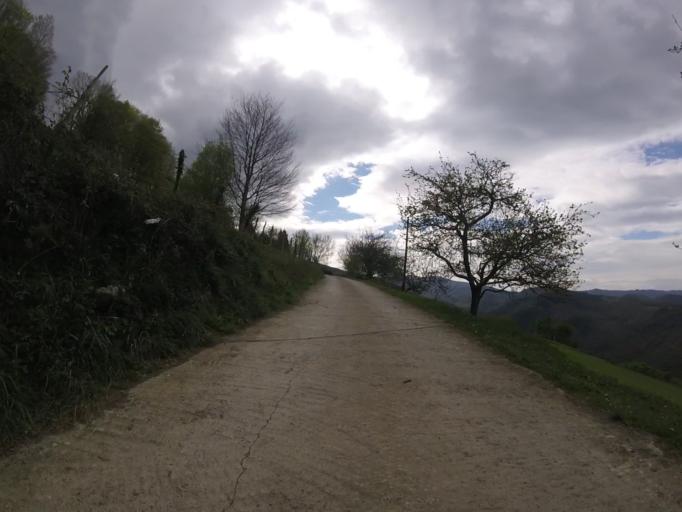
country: ES
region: Basque Country
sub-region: Provincia de Guipuzcoa
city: Aizarnazabal
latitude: 43.2521
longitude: -2.2070
